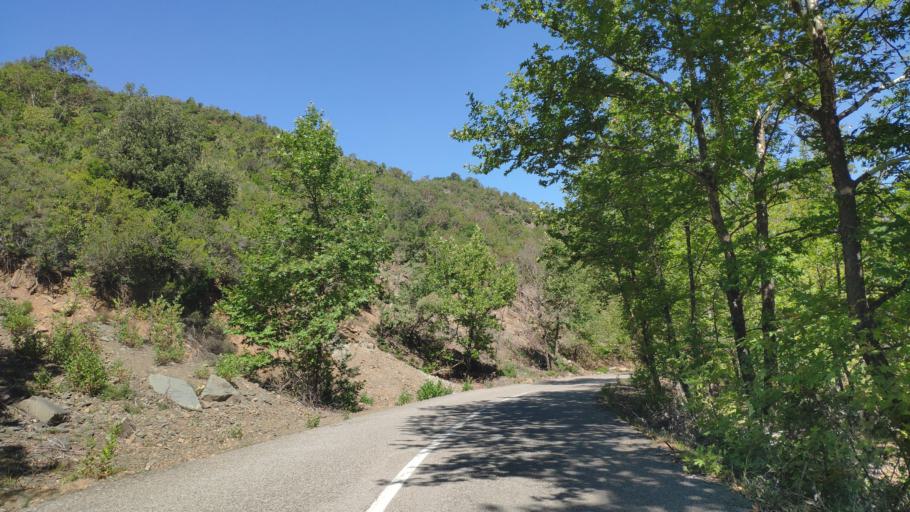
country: GR
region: Central Greece
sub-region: Nomos Evrytanias
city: Kerasochori
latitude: 38.9950
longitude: 21.5140
